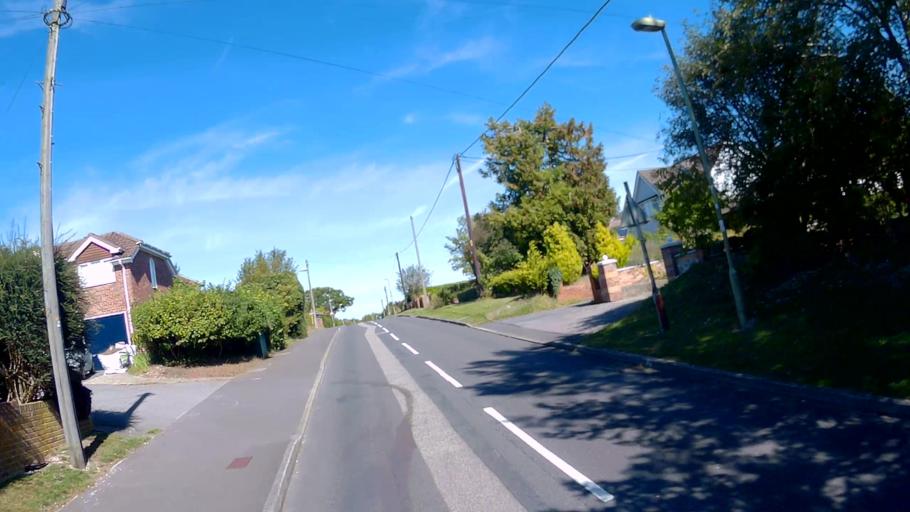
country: GB
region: England
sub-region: Hampshire
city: Basingstoke
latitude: 51.2560
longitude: -1.1379
